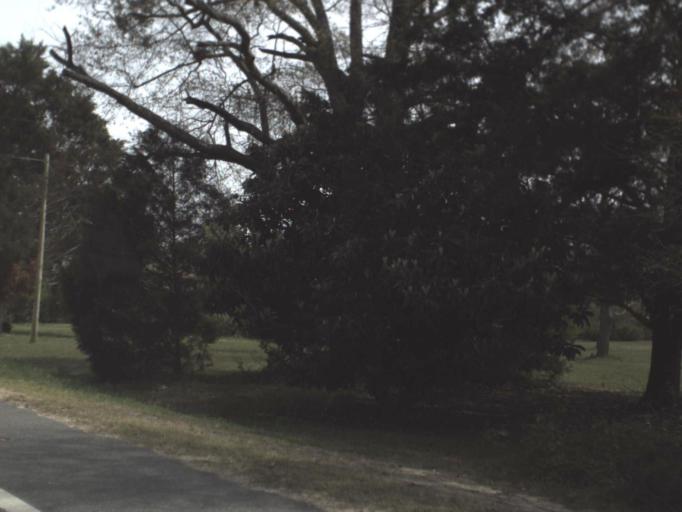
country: US
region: Florida
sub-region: Jackson County
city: Graceville
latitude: 30.9637
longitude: -85.5672
